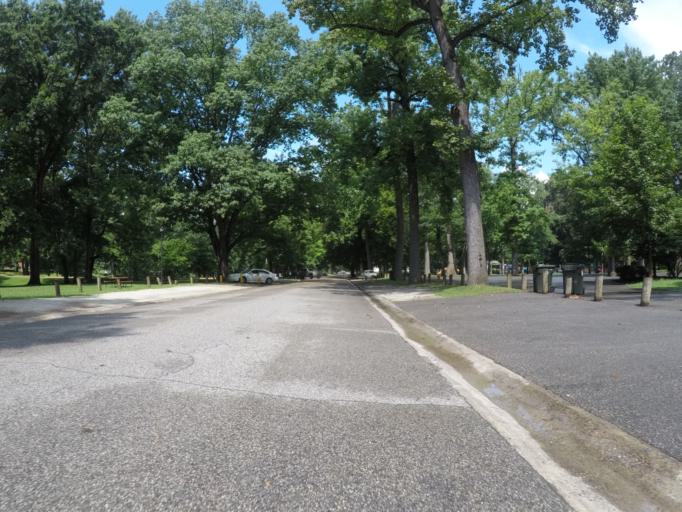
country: US
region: Kentucky
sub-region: Boyd County
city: Ashland
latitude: 38.4729
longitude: -82.6385
